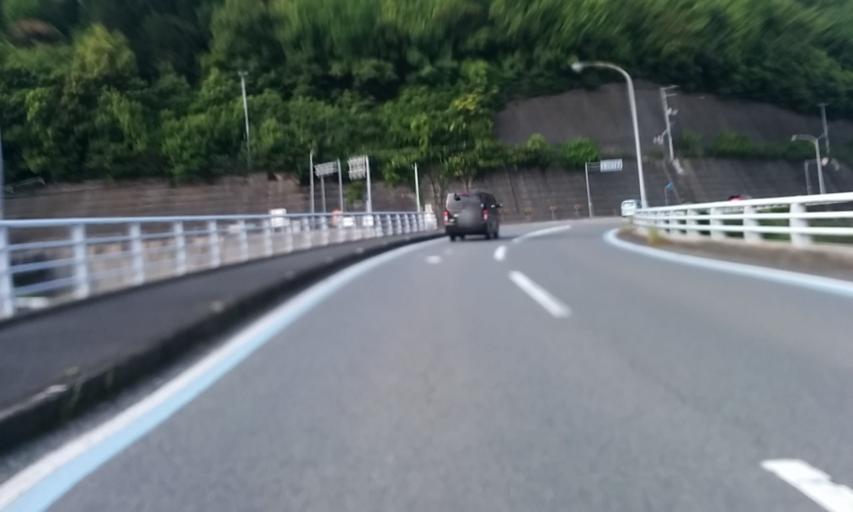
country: JP
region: Ehime
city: Saijo
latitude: 33.8873
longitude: 133.1831
